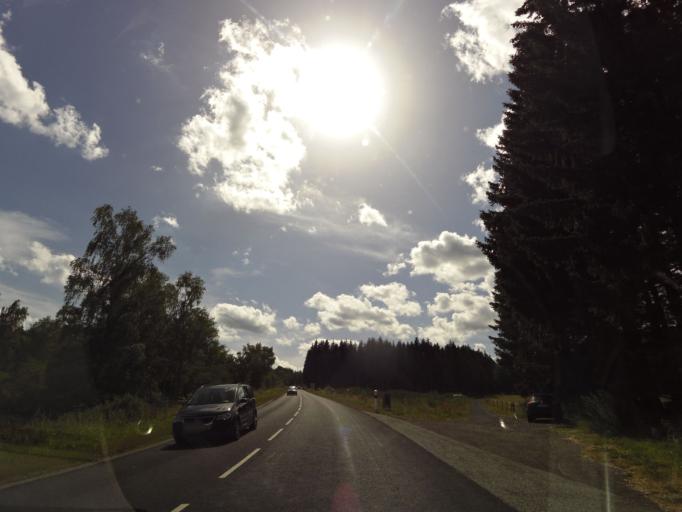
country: FR
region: Auvergne
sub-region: Departement du Puy-de-Dome
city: Orcines
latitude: 45.7601
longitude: 2.9813
